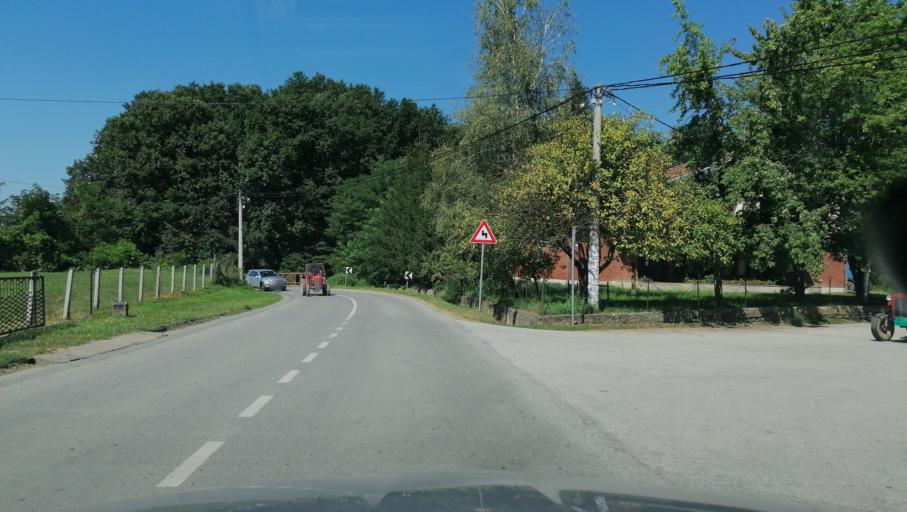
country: RS
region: Central Serbia
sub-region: Raski Okrug
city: Vrnjacka Banja
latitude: 43.6903
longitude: 20.8690
